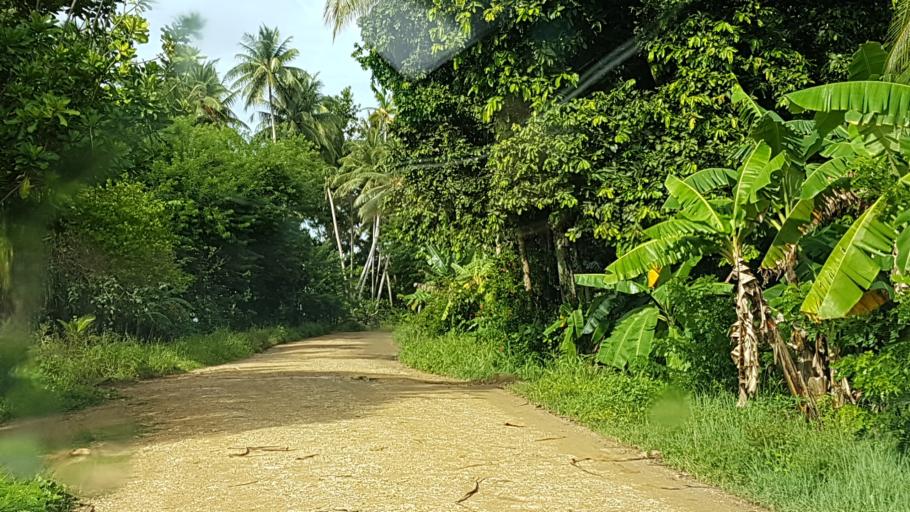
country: PG
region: Milne Bay
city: Alotau
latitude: -10.2744
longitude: 150.7900
